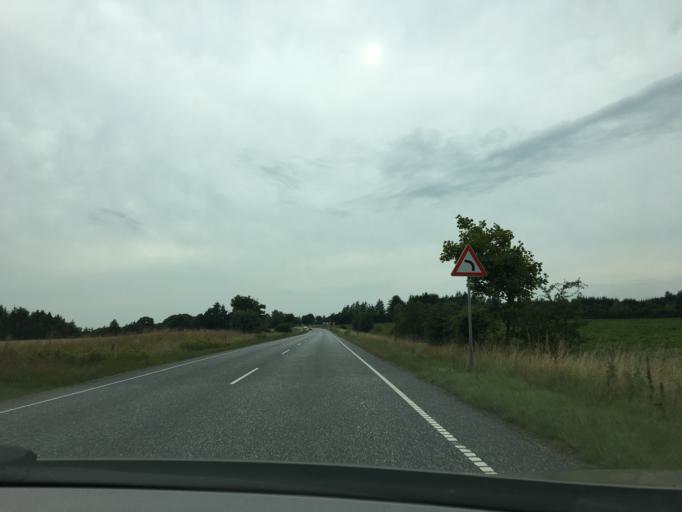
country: DK
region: Central Jutland
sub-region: Herning Kommune
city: Vildbjerg
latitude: 56.1142
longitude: 8.7685
